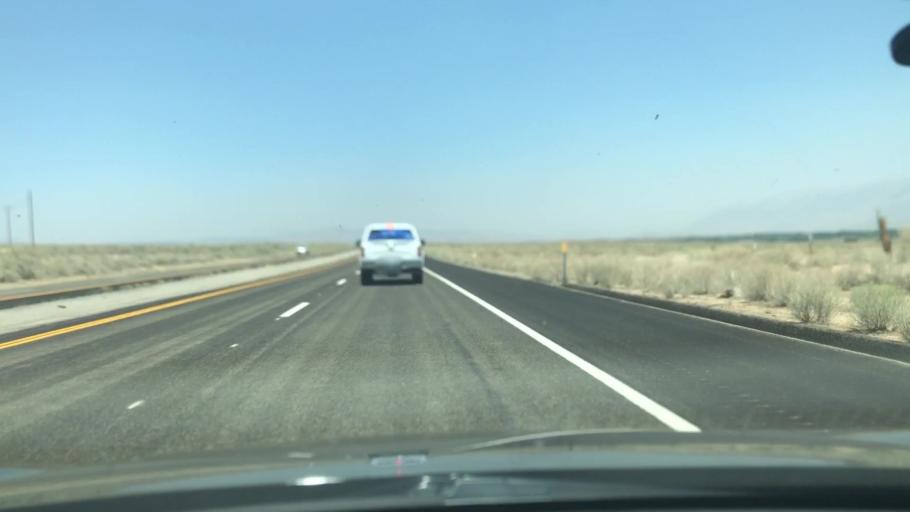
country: US
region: California
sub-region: Inyo County
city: Bishop
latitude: 37.3042
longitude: -118.3802
